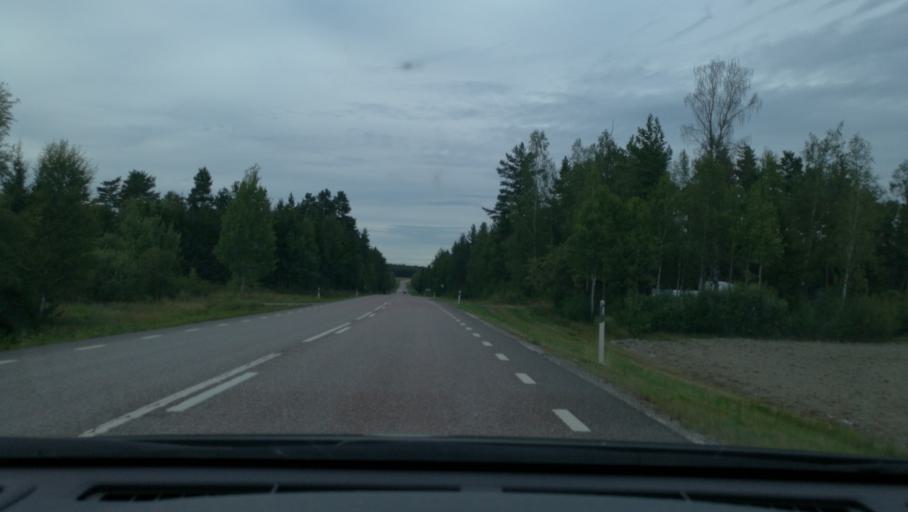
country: SE
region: Soedermanland
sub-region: Katrineholms Kommun
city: Katrineholm
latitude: 59.0445
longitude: 16.2201
